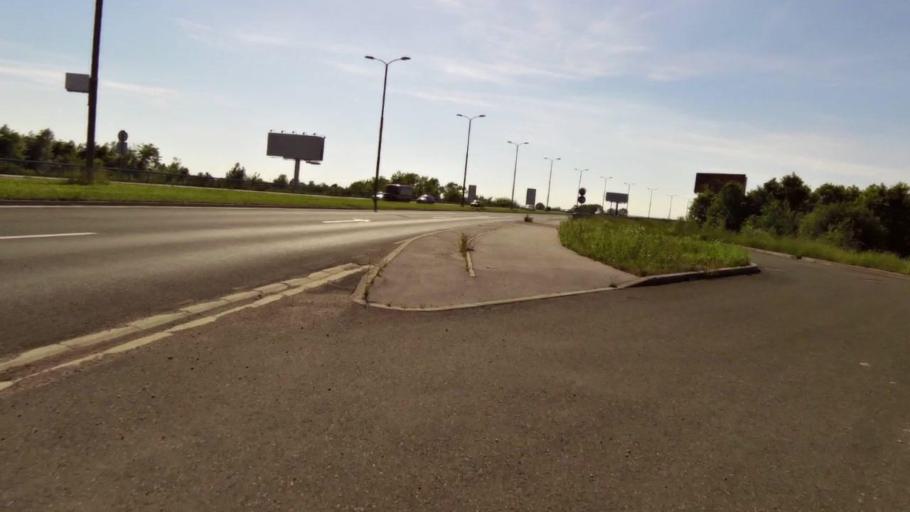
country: HR
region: Zagrebacka
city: Micevec
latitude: 45.7677
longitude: 16.0762
